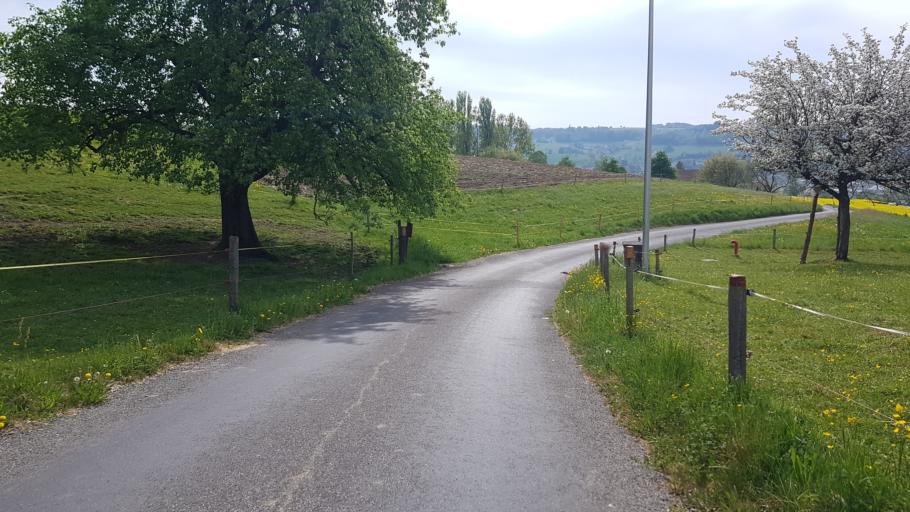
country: CH
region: Aargau
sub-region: Bezirk Kulm
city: Gontenschwil
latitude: 47.2848
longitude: 8.1640
